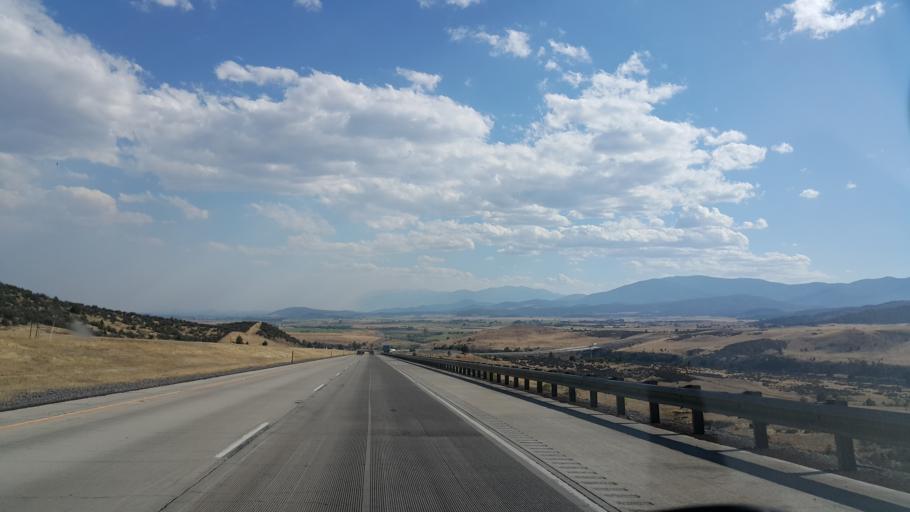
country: US
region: California
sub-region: Siskiyou County
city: Yreka
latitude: 41.7833
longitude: -122.5845
